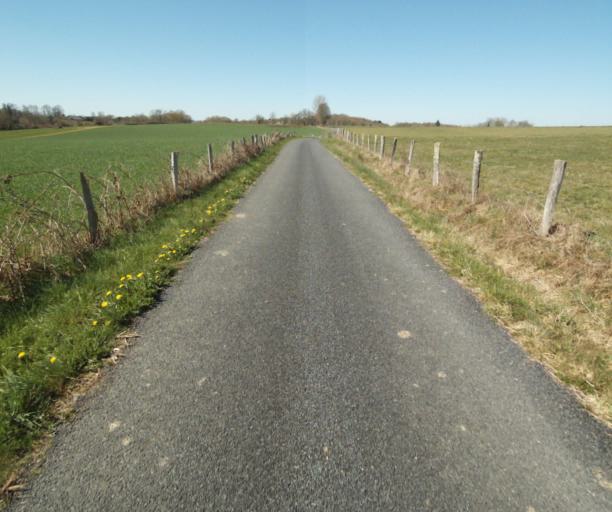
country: FR
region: Limousin
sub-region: Departement de la Correze
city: Chamboulive
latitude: 45.4572
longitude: 1.6958
